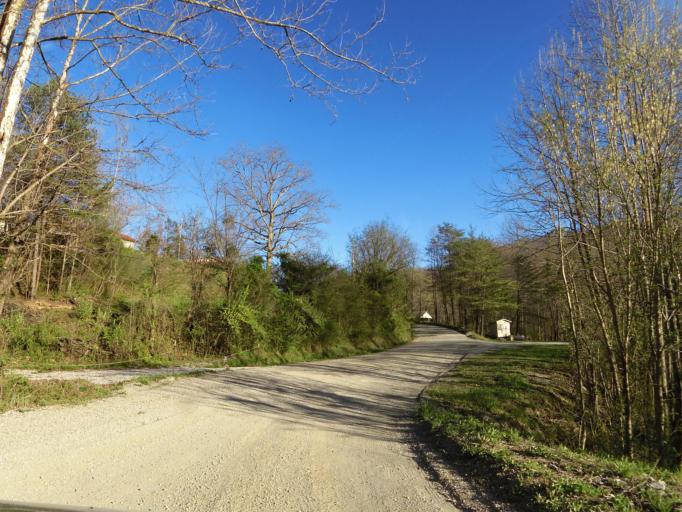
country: US
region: Tennessee
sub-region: Campbell County
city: Caryville
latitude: 36.2870
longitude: -84.3621
